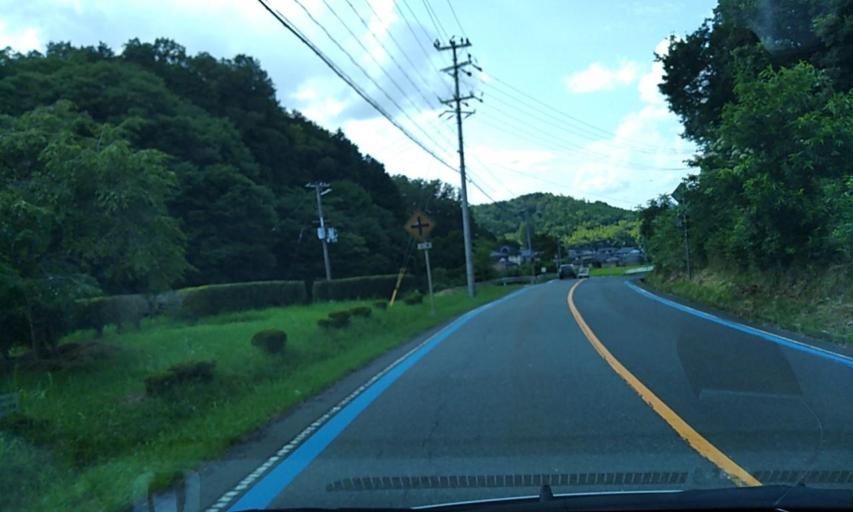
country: JP
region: Kyoto
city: Ayabe
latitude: 35.3075
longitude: 135.2835
